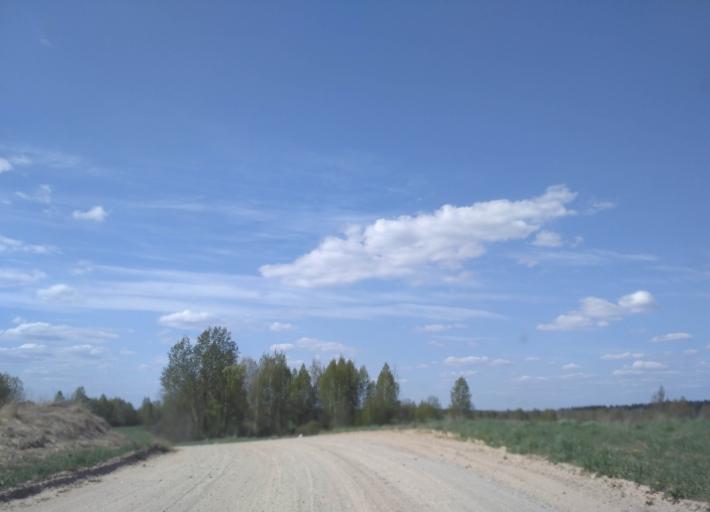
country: BY
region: Minsk
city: Narach
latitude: 54.9707
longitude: 26.6344
